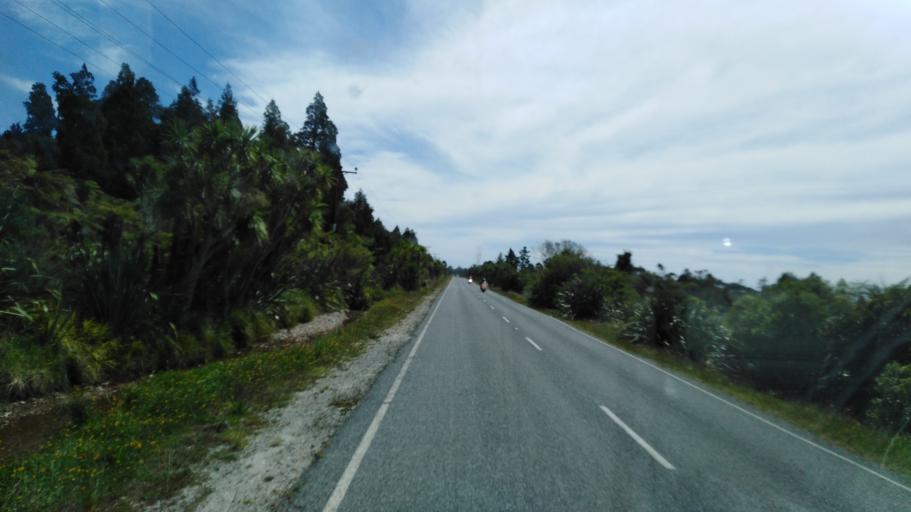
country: NZ
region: West Coast
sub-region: Buller District
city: Westport
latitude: -41.7437
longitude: 171.7156
